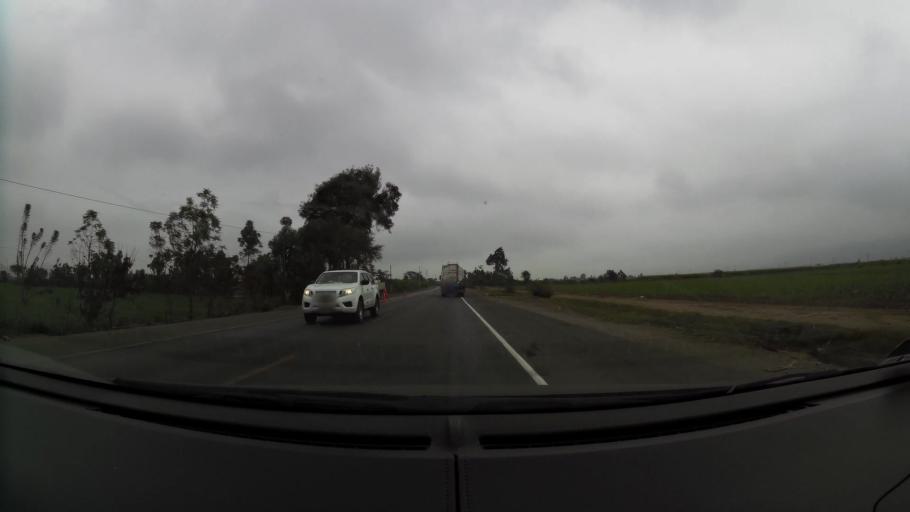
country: PE
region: La Libertad
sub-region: Viru
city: Viru
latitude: -8.4389
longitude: -78.7577
